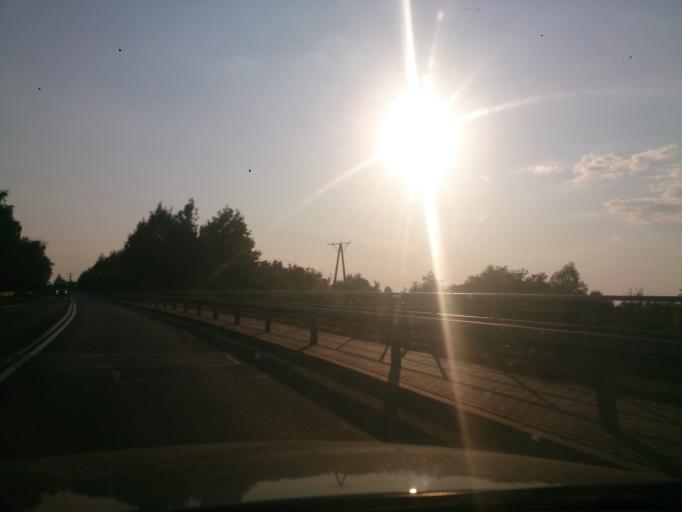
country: PL
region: Subcarpathian Voivodeship
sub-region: Powiat kolbuszowski
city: Majdan Krolewski
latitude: 50.3688
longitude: 21.7399
